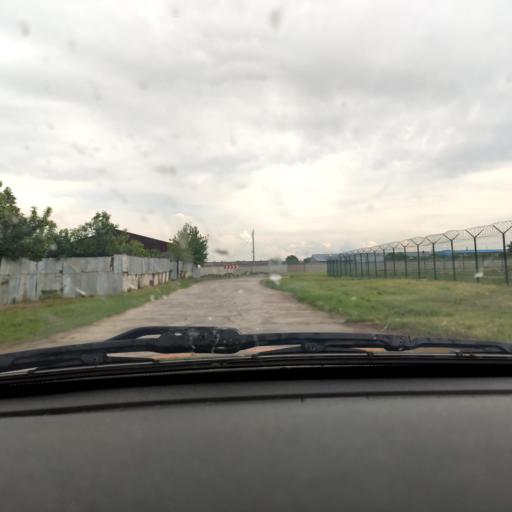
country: RU
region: Samara
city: Tol'yatti
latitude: 53.5349
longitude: 49.4685
